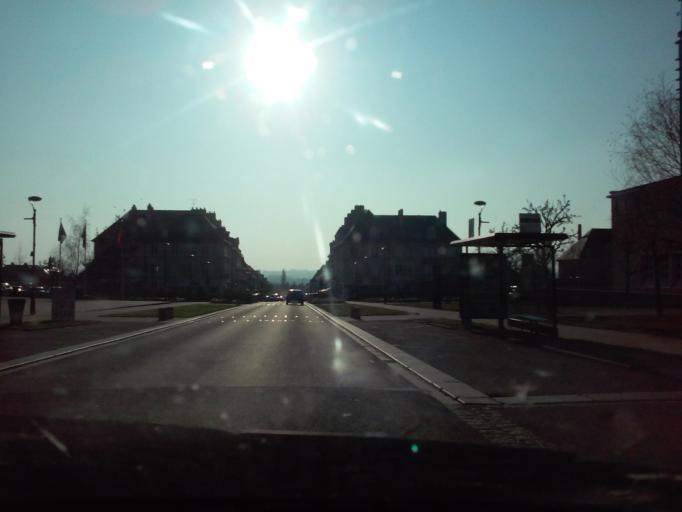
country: FR
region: Lower Normandy
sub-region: Departement du Calvados
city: Villers-Bocage
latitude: 49.0806
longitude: -0.6547
